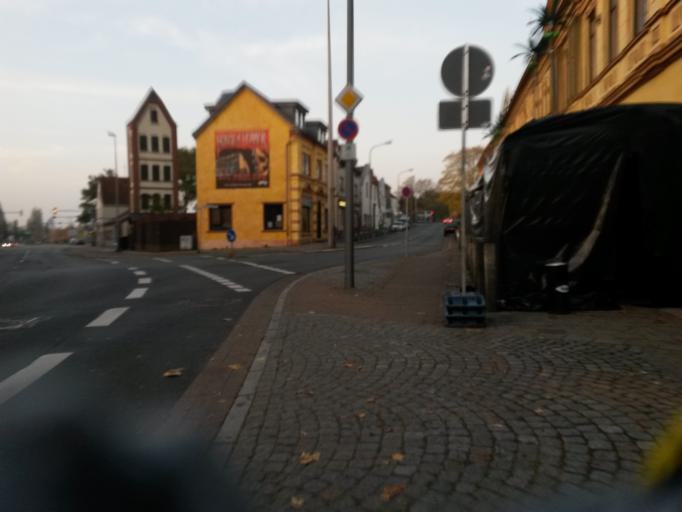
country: DE
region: Bremen
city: Bremen
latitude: 53.0556
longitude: 8.8849
